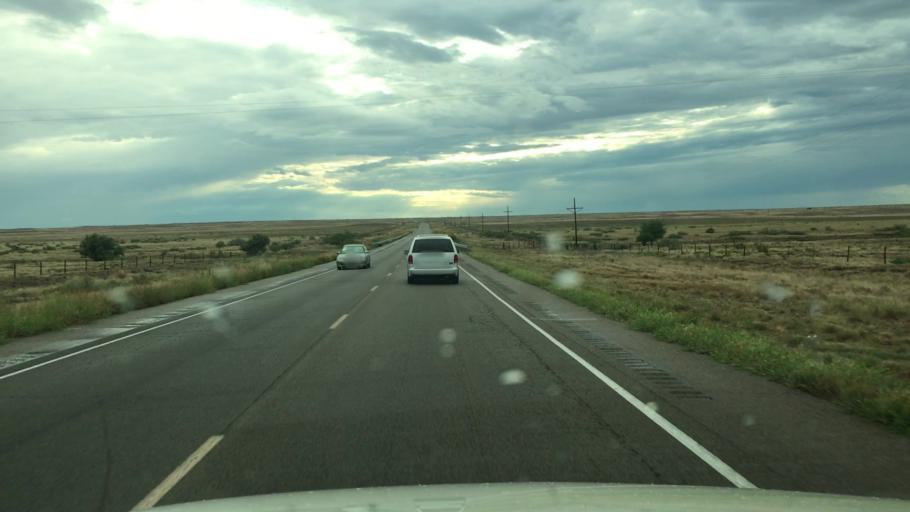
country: US
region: New Mexico
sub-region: Chaves County
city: Dexter
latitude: 33.4067
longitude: -104.2995
